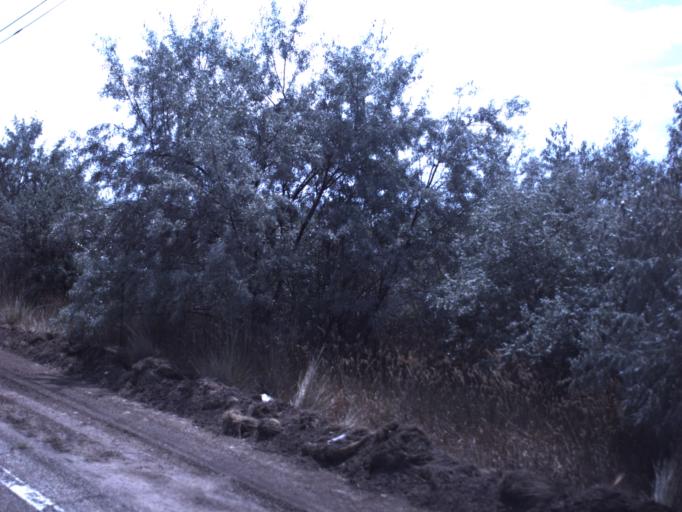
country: US
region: Utah
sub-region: Duchesne County
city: Roosevelt
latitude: 40.3548
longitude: -110.0297
